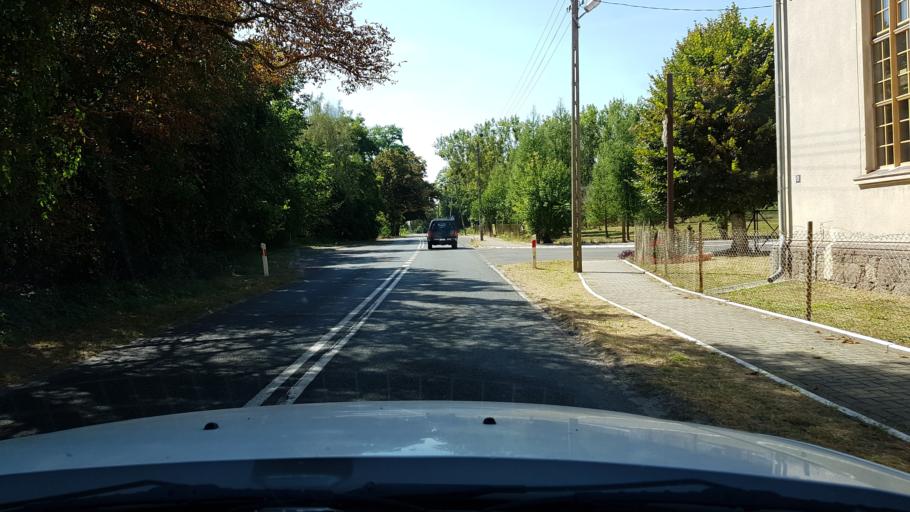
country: PL
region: West Pomeranian Voivodeship
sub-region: Powiat gryfinski
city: Cedynia
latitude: 52.8332
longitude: 14.1919
